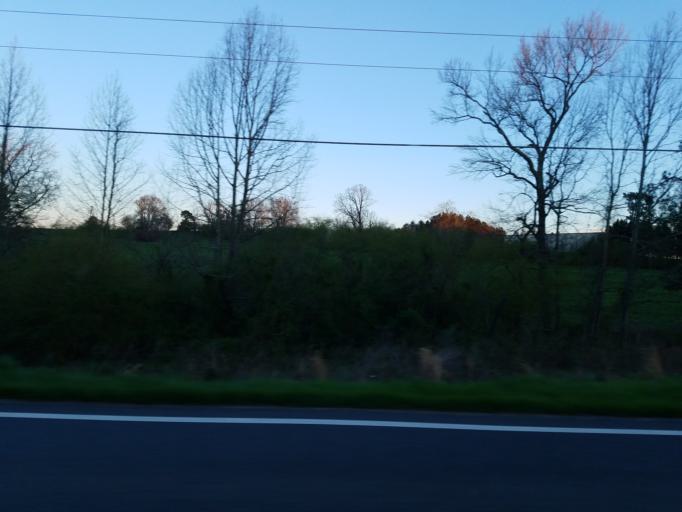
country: US
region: Georgia
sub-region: Forsyth County
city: Cumming
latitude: 34.2628
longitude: -84.0655
